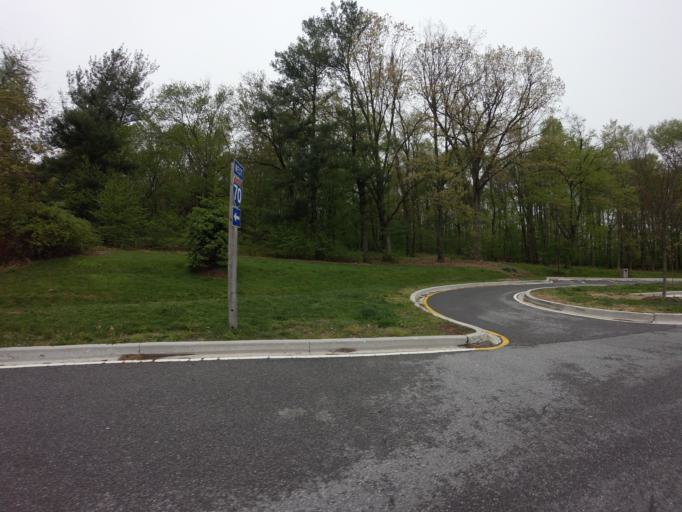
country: US
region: Maryland
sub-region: Frederick County
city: Myersville
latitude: 39.5246
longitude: -77.5998
